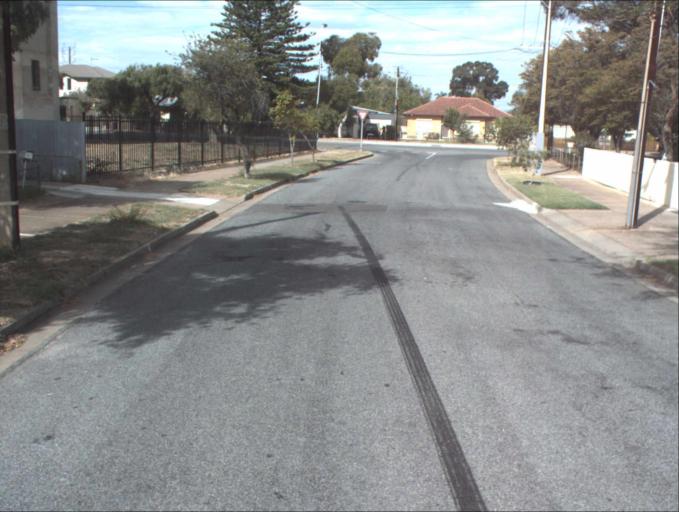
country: AU
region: South Australia
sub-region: Port Adelaide Enfield
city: Birkenhead
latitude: -34.7973
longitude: 138.4958
